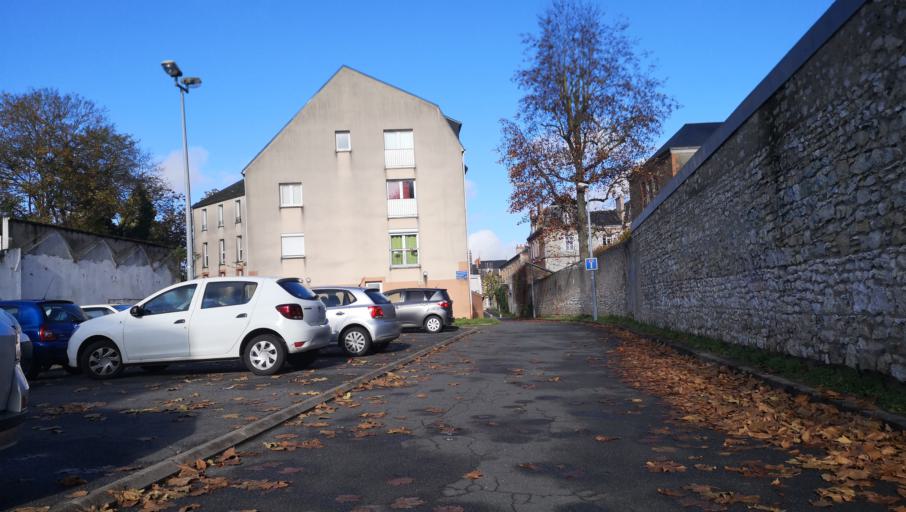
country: FR
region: Centre
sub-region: Departement du Loiret
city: Saint-Jean-le-Blanc
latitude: 47.9009
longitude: 1.9273
